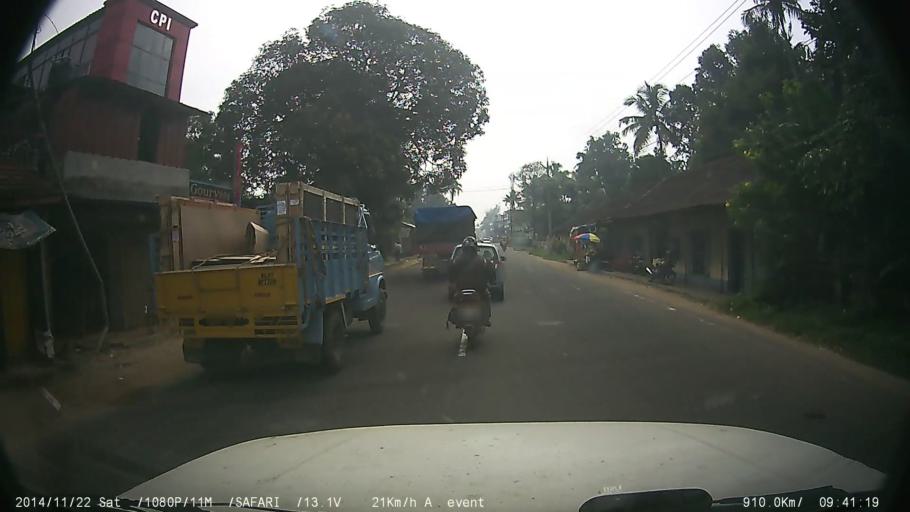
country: IN
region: Kerala
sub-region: Ernakulam
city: Perumpavur
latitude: 10.1544
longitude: 76.4484
